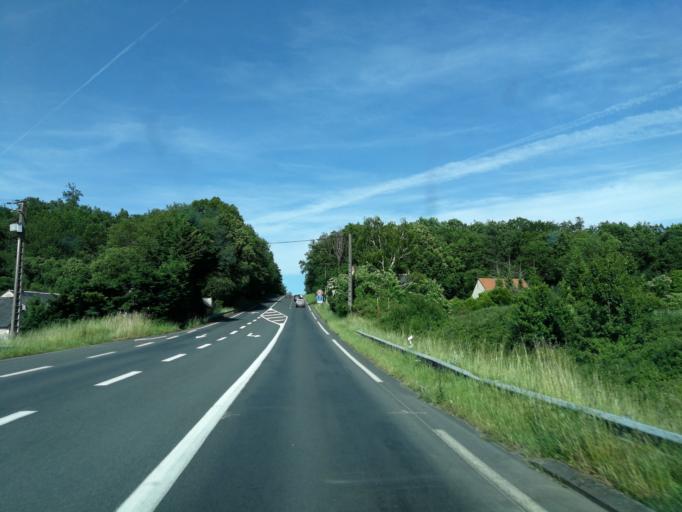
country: FR
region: Centre
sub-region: Departement d'Indre-et-Loire
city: Huismes
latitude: 47.2003
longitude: 0.3201
